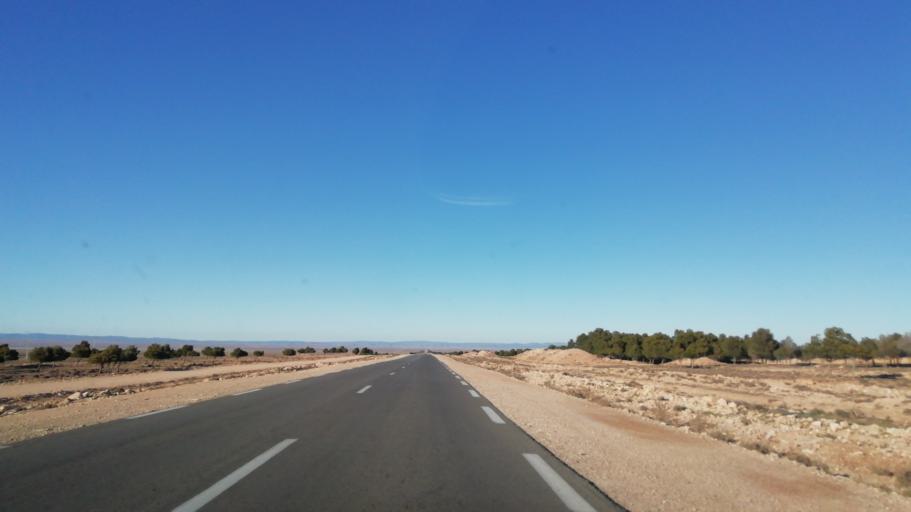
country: DZ
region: Tlemcen
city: Sebdou
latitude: 34.2872
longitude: -1.2598
